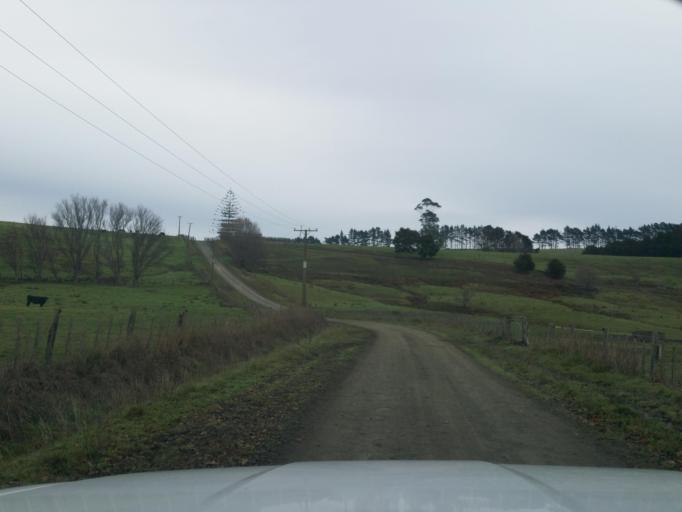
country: NZ
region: Northland
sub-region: Whangarei
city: Maungatapere
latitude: -35.7996
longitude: 174.0525
